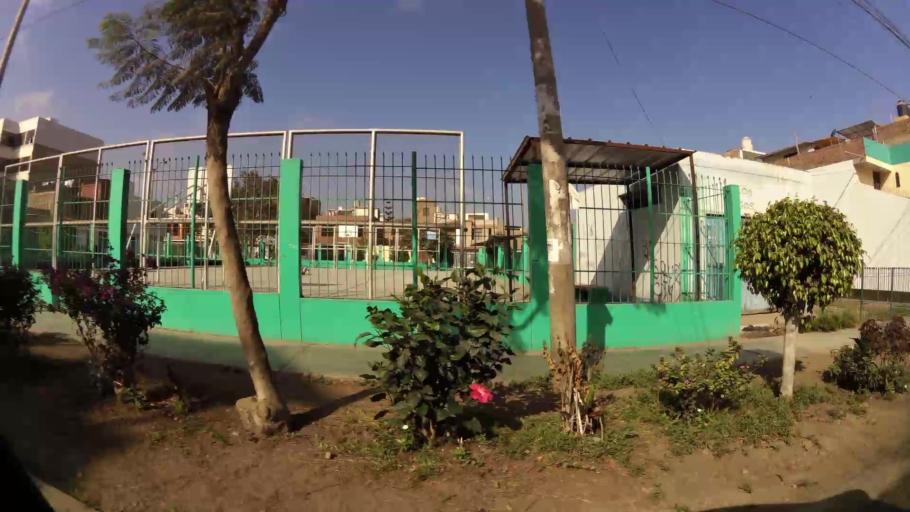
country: PE
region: La Libertad
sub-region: Provincia de Trujillo
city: Trujillo
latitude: -8.1110
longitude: -79.0060
